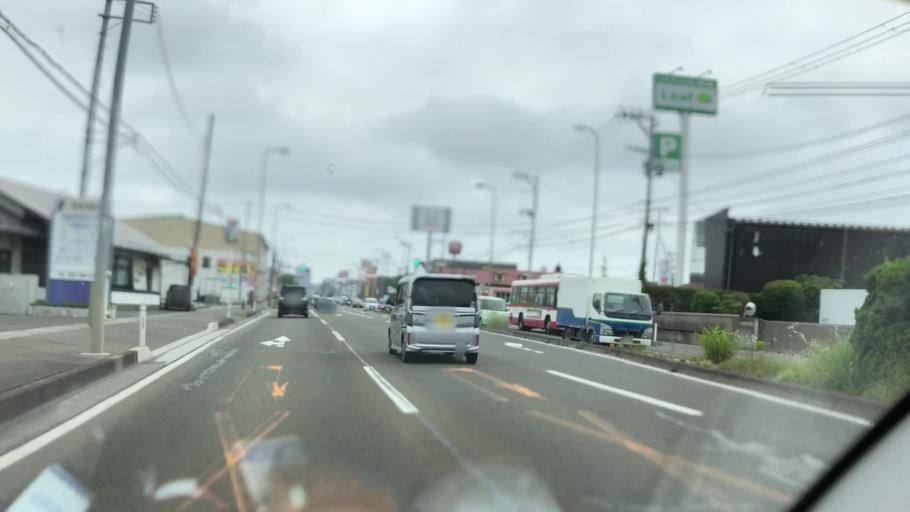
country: JP
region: Miyagi
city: Rifu
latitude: 38.2693
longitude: 140.9457
